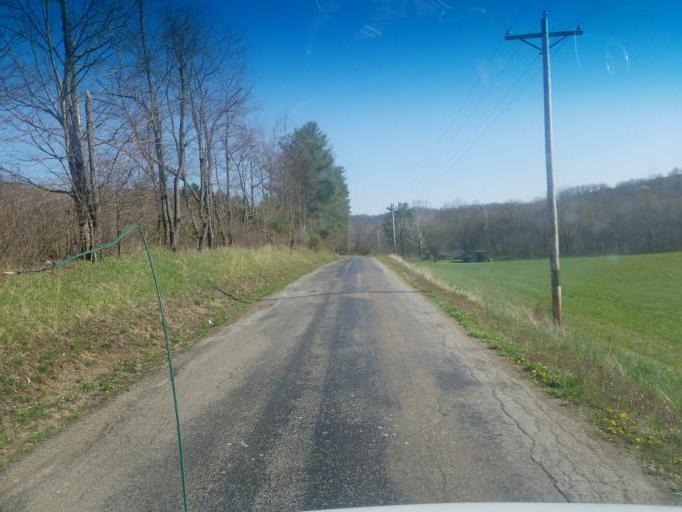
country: US
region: Ohio
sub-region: Muskingum County
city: Frazeysburg
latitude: 40.2380
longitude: -82.1952
